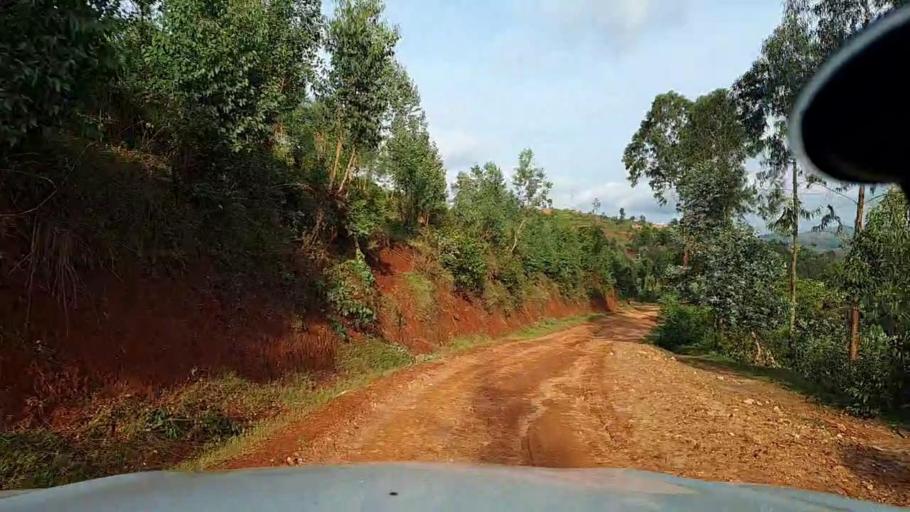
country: RW
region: Southern Province
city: Gitarama
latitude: -2.1861
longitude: 29.5681
